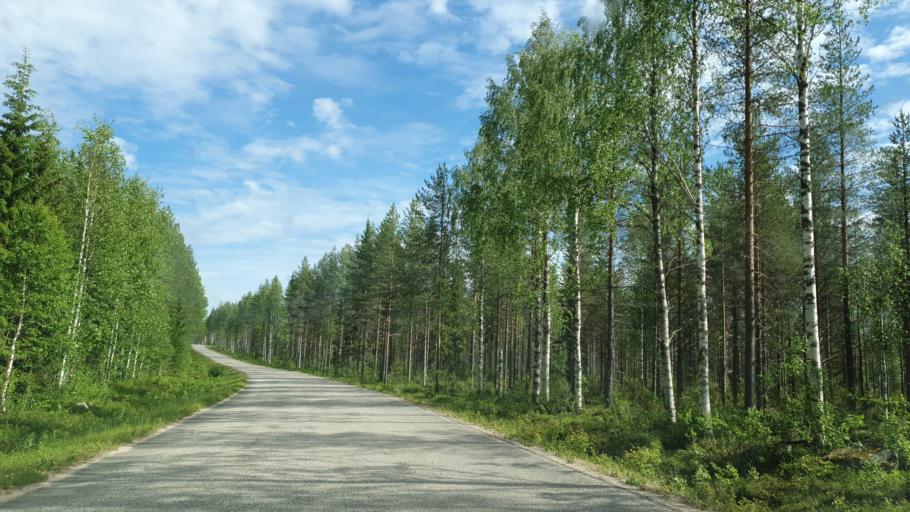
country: FI
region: Kainuu
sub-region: Kehys-Kainuu
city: Kuhmo
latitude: 64.5189
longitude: 29.3830
